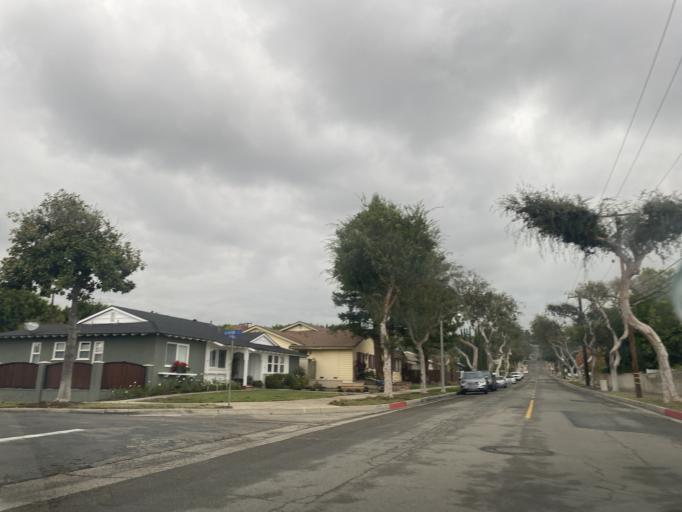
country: US
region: California
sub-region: Orange County
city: Fullerton
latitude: 33.8792
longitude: -117.9071
